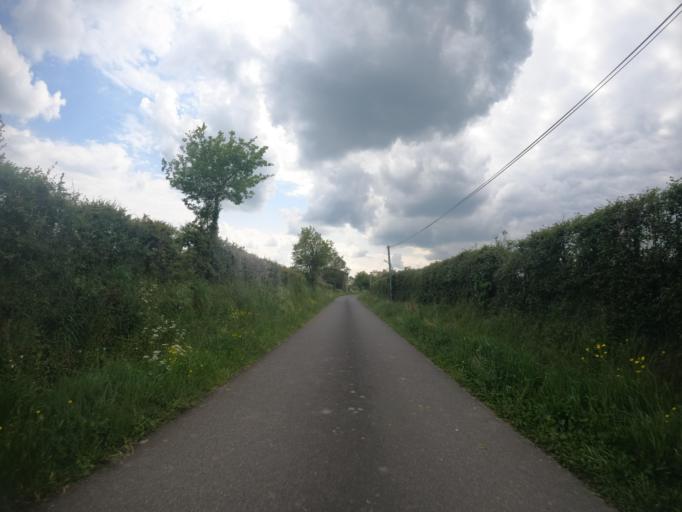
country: FR
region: Poitou-Charentes
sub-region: Departement des Deux-Sevres
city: Saint-Varent
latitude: 46.8681
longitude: -0.3048
